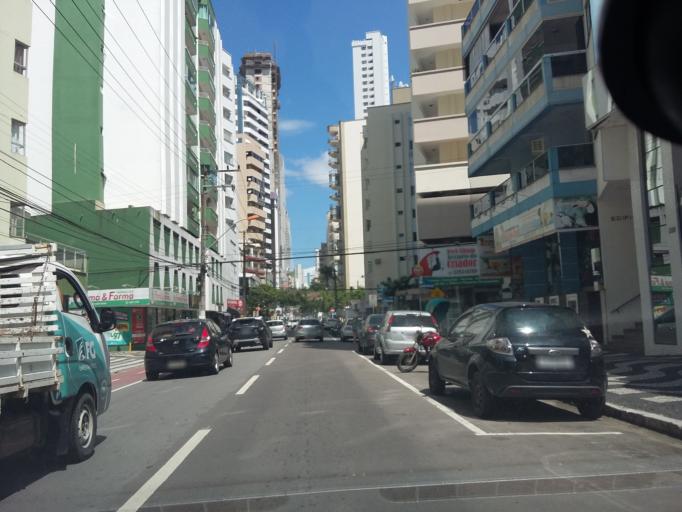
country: BR
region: Santa Catarina
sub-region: Balneario Camboriu
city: Balneario Camboriu
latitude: -26.9768
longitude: -48.6371
